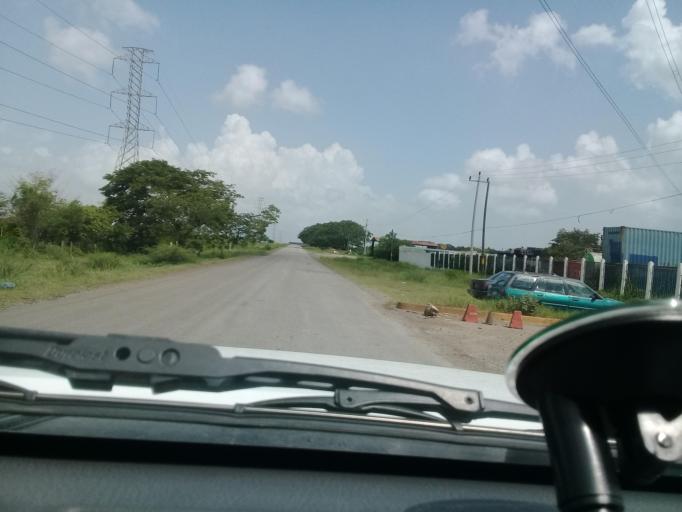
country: MX
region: Veracruz
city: Moralillo
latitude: 22.2254
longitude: -98.0112
